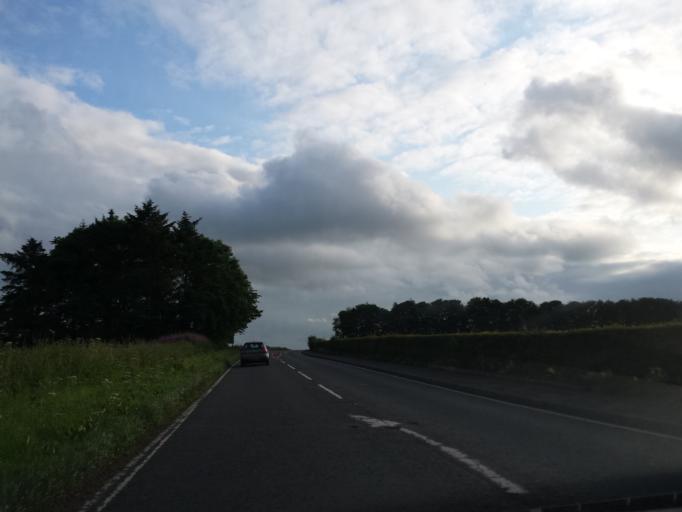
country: GB
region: Scotland
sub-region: Fife
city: Ceres
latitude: 56.3393
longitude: -2.9617
